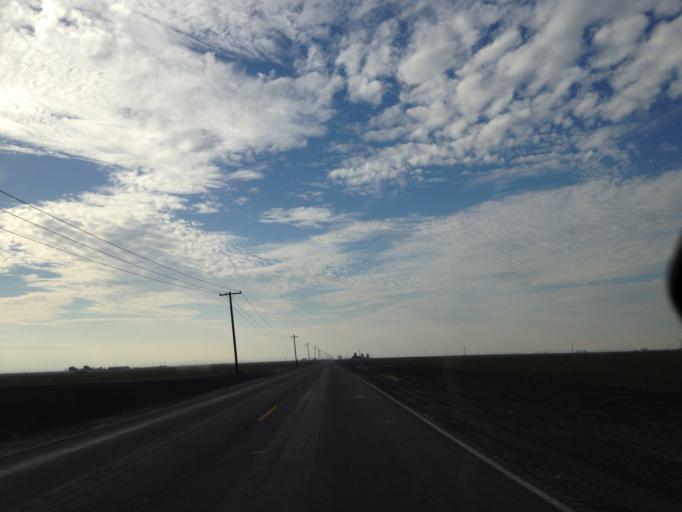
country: US
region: California
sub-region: Kern County
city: Buttonwillow
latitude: 35.4423
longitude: -119.5039
